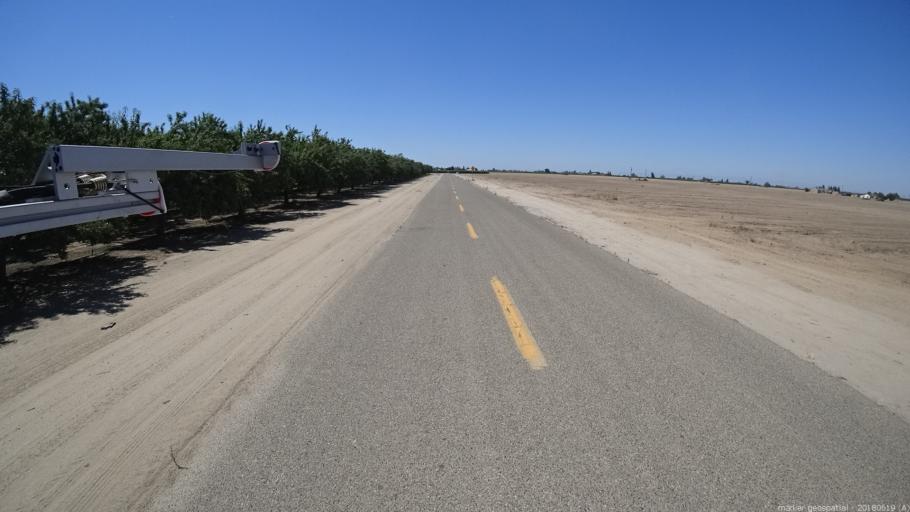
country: US
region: California
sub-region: Fresno County
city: Biola
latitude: 36.8392
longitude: -120.0649
